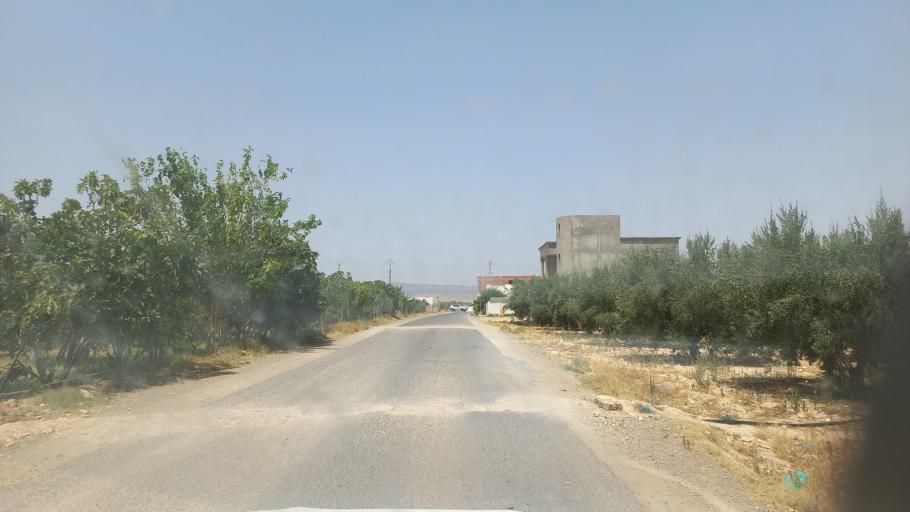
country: TN
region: Al Qasrayn
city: Kasserine
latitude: 35.2527
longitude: 9.0178
